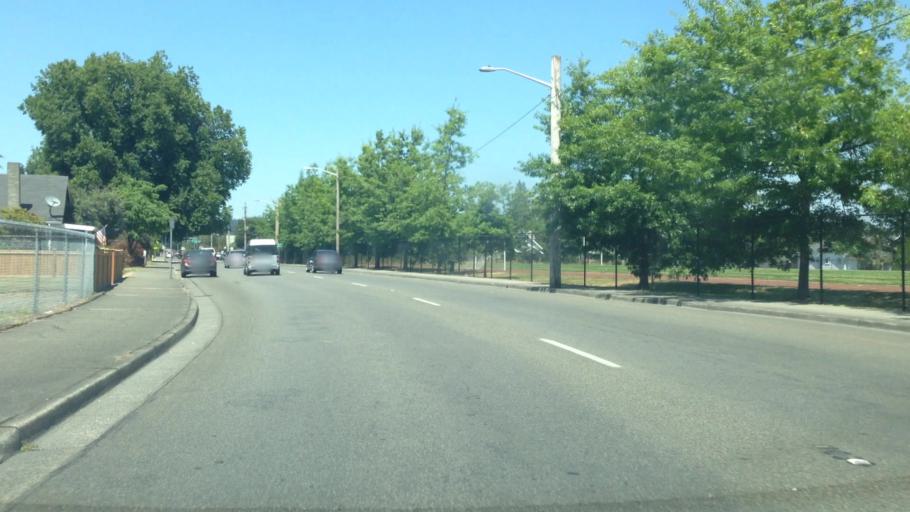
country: US
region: Washington
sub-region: Pierce County
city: Puyallup
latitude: 47.1867
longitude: -122.2914
